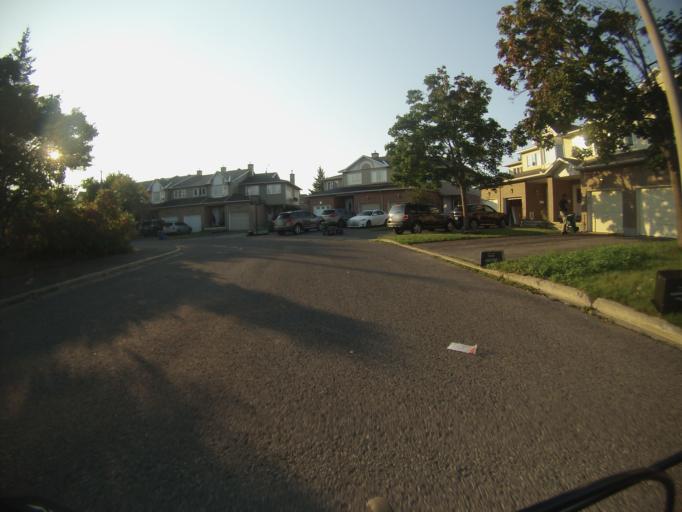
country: CA
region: Ontario
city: Ottawa
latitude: 45.3601
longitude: -75.6332
